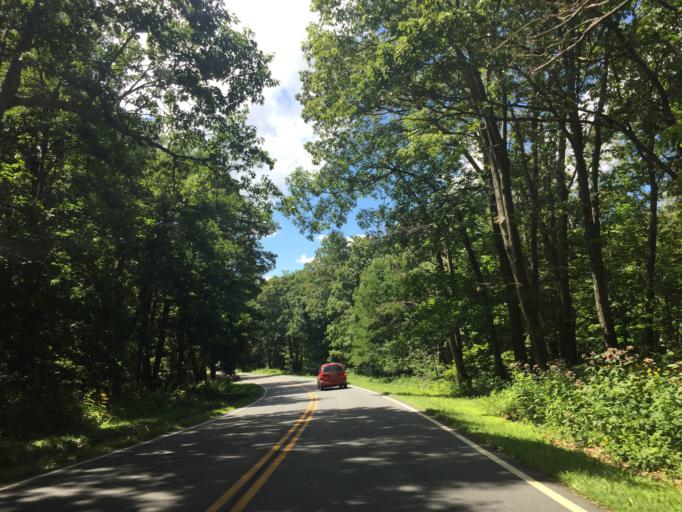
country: US
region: Virginia
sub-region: Rappahannock County
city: Washington
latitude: 38.7680
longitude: -78.2326
